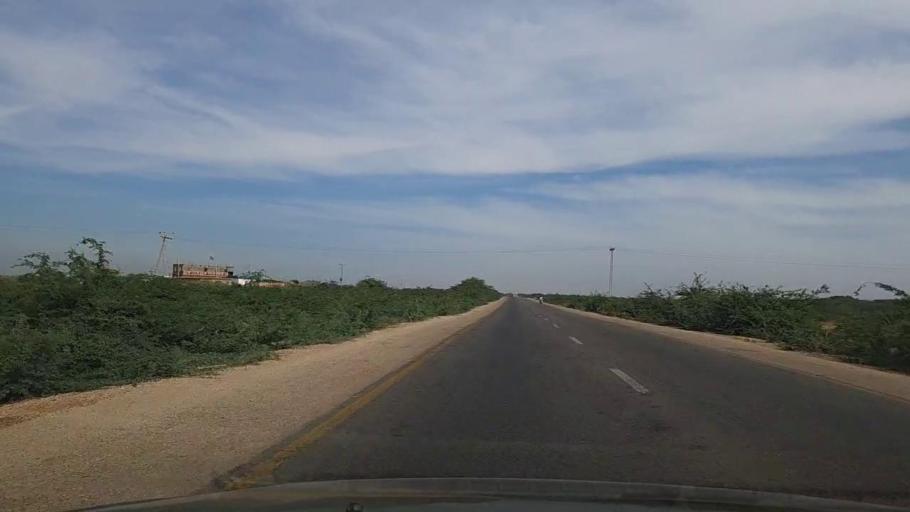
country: PK
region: Sindh
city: Thatta
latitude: 24.8401
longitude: 68.0050
